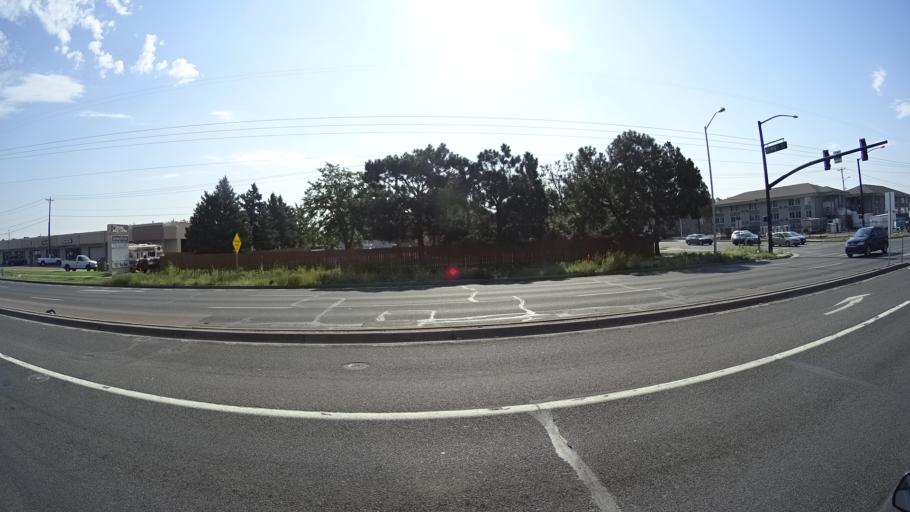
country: US
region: Colorado
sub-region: El Paso County
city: Stratmoor
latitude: 38.7847
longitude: -104.7576
